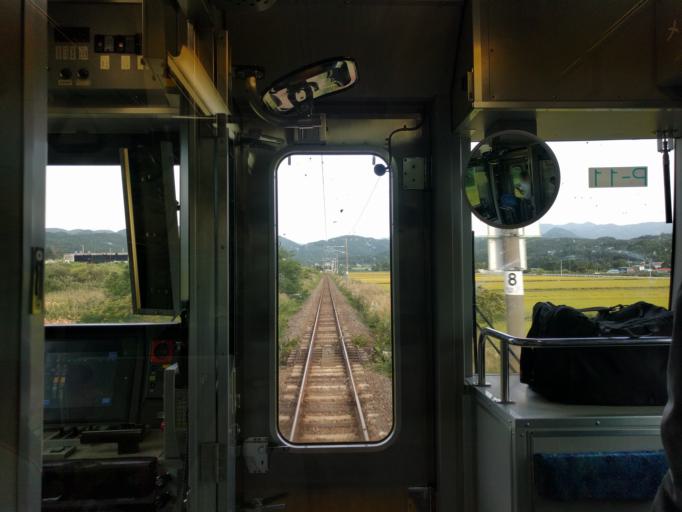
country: JP
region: Fukushima
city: Motomiya
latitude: 37.4755
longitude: 140.3005
